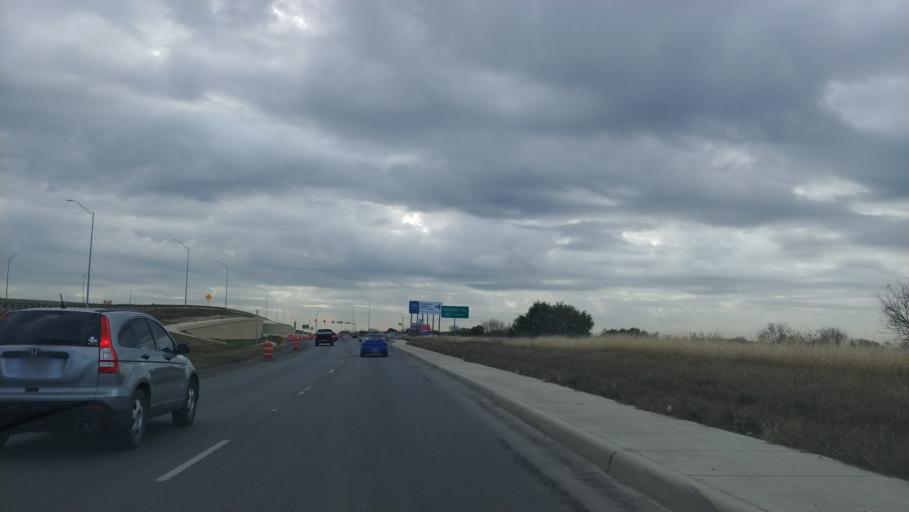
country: US
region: Texas
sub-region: Bexar County
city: Lackland Air Force Base
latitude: 29.4055
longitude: -98.7091
